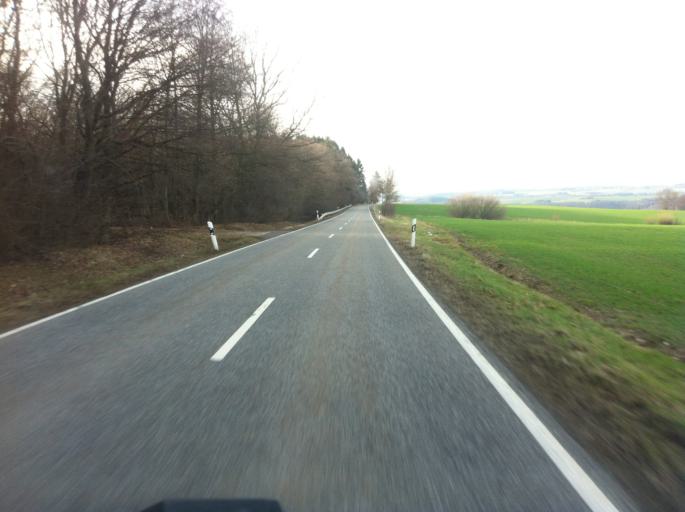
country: DE
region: Rheinland-Pfalz
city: Wurrich
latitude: 49.9737
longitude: 7.2922
